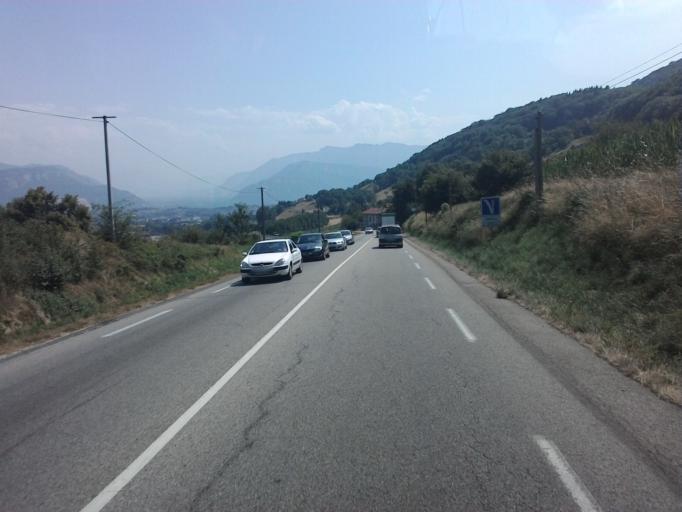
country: FR
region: Rhone-Alpes
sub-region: Departement de l'Isere
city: Chirens
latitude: 45.3961
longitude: 5.5698
